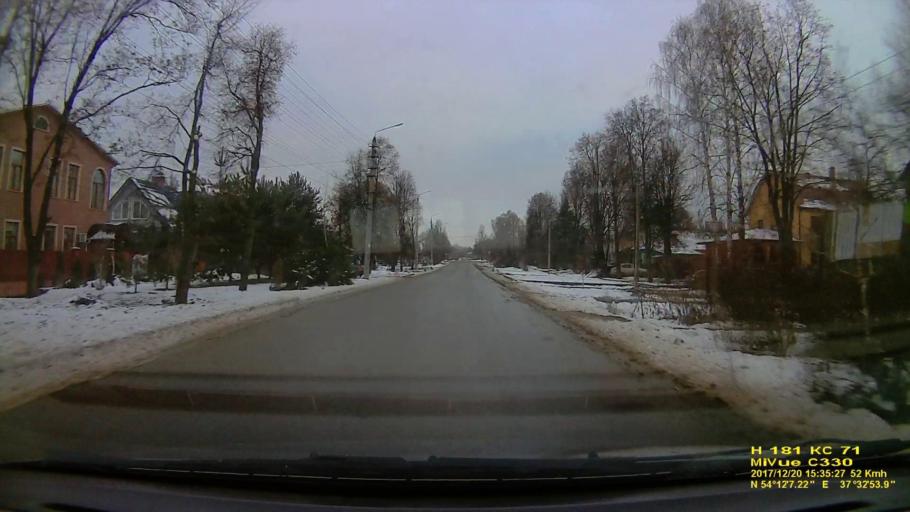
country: RU
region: Tula
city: Tula
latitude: 54.2019
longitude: 37.5484
